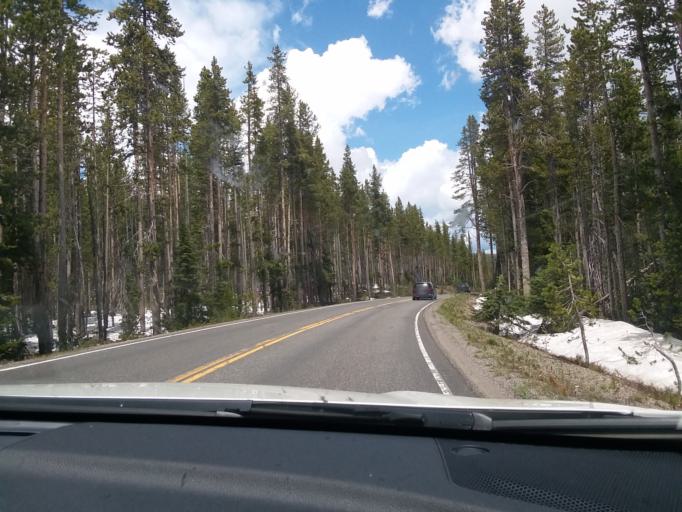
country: US
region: Montana
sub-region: Gallatin County
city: West Yellowstone
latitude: 44.2003
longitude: -110.6598
